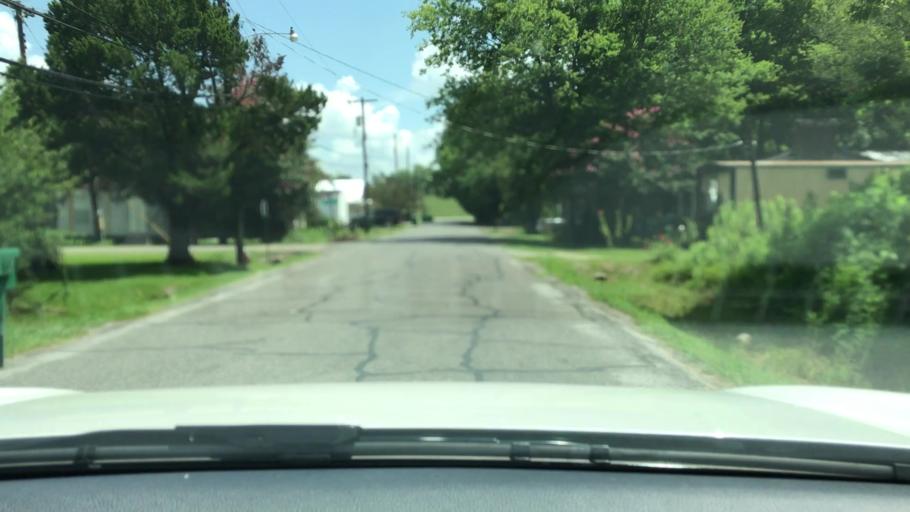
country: US
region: Louisiana
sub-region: Iberville Parish
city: Plaquemine
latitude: 30.2805
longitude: -91.2248
